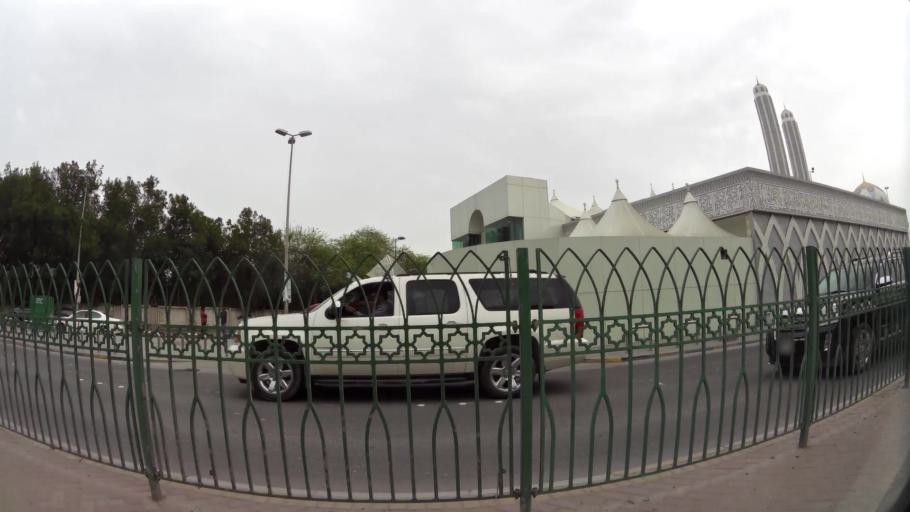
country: BH
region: Manama
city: Jidd Hafs
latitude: 26.2042
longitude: 50.5343
